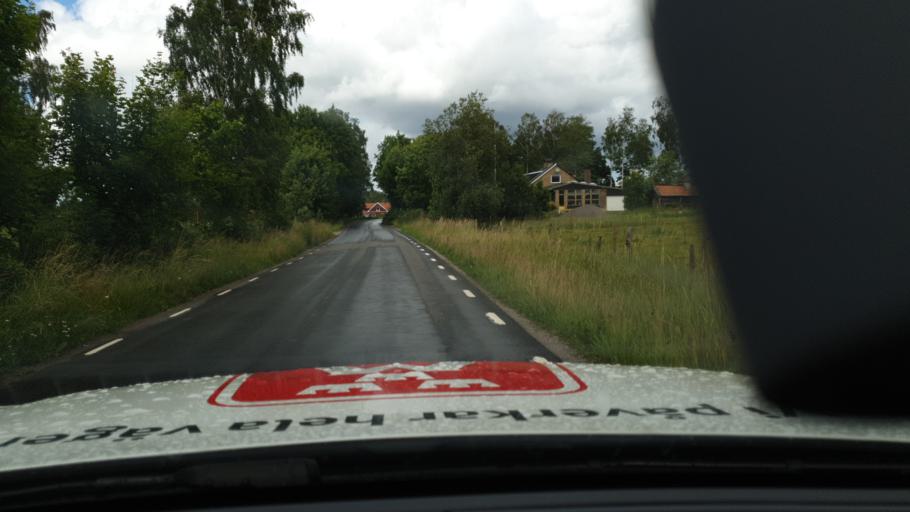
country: SE
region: Vaestra Goetaland
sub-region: Falkopings Kommun
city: Akarp
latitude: 58.2650
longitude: 13.5970
